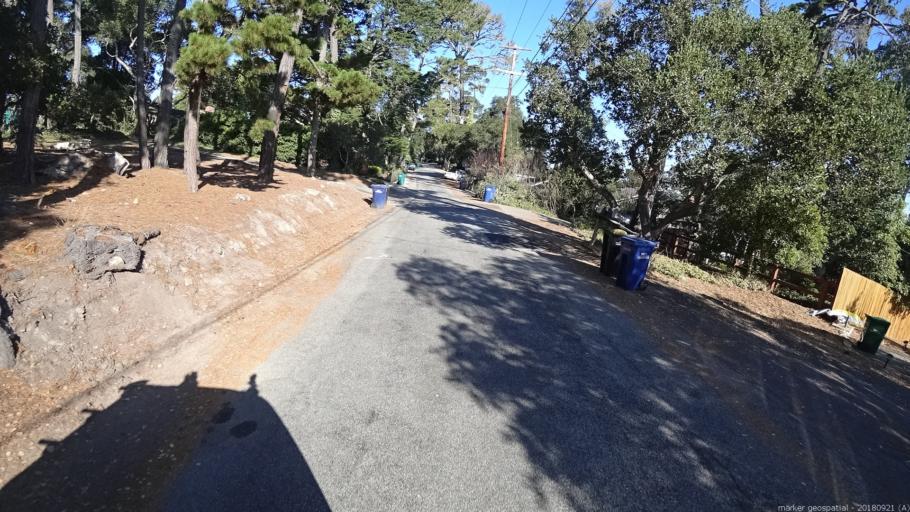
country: US
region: California
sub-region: Monterey County
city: Carmel-by-the-Sea
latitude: 36.5695
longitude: -121.9142
